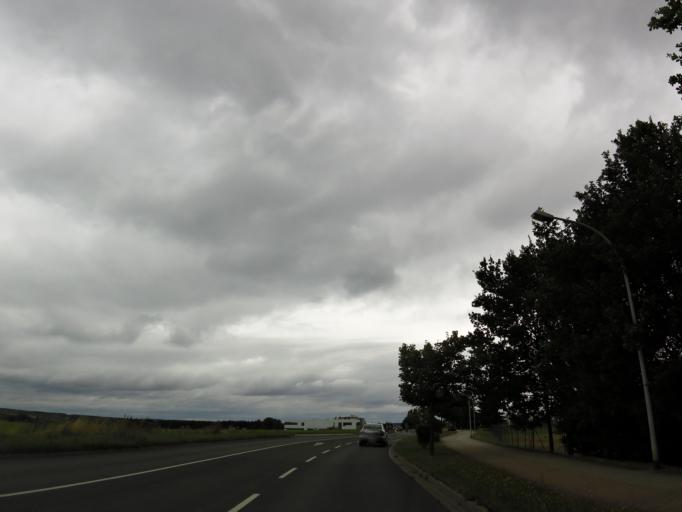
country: DE
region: Thuringia
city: Hermsdorf
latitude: 50.8902
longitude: 11.8474
